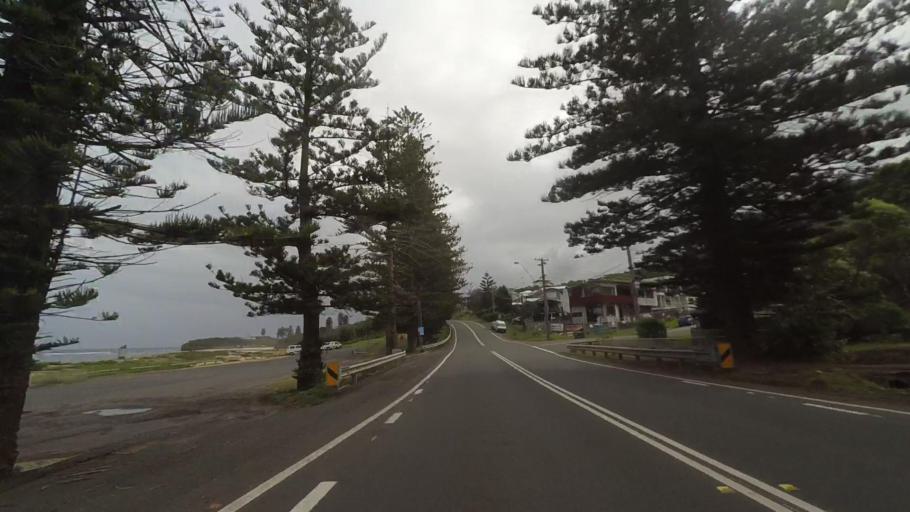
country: AU
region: New South Wales
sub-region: Wollongong
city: Bulli
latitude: -34.2941
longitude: 150.9435
